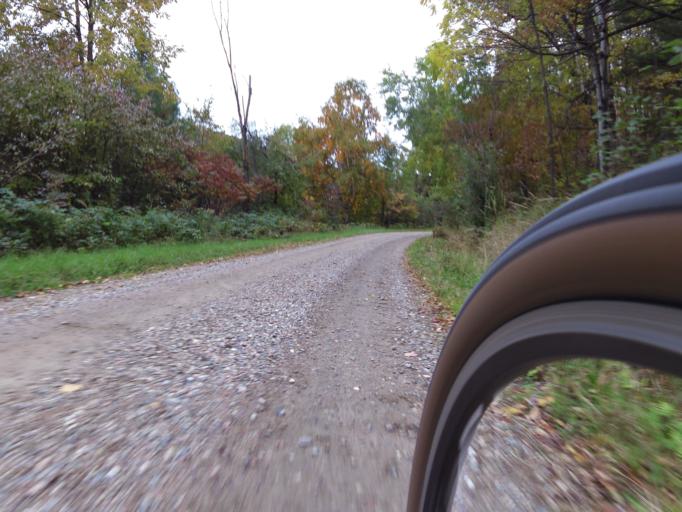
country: CA
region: Quebec
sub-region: Outaouais
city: Wakefield
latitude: 45.6031
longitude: -76.0264
